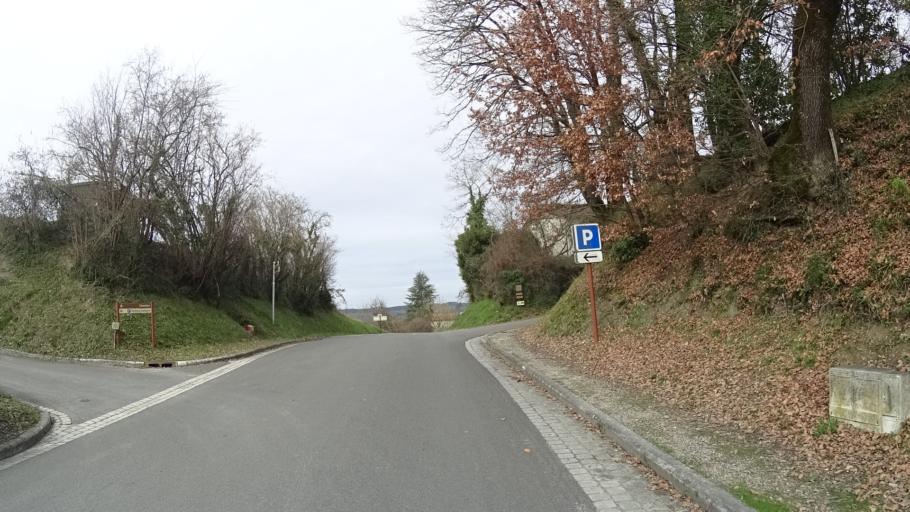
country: FR
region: Aquitaine
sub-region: Departement de la Dordogne
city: Saint-Aulaye
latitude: 45.2735
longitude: 0.1679
